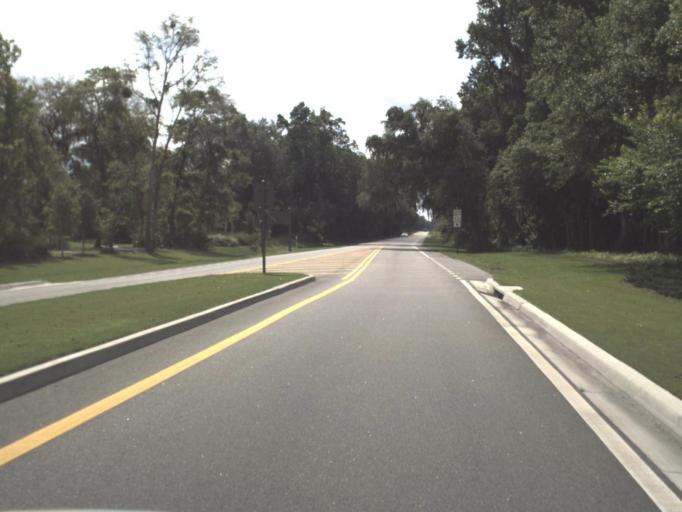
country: US
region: Florida
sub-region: Clay County
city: Green Cove Springs
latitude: 30.0201
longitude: -81.6387
